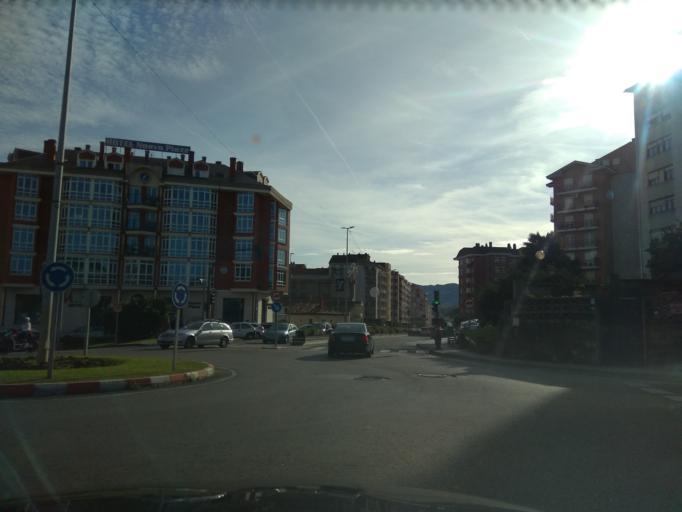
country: ES
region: Cantabria
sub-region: Provincia de Cantabria
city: El Astillero
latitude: 43.4202
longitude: -3.8465
